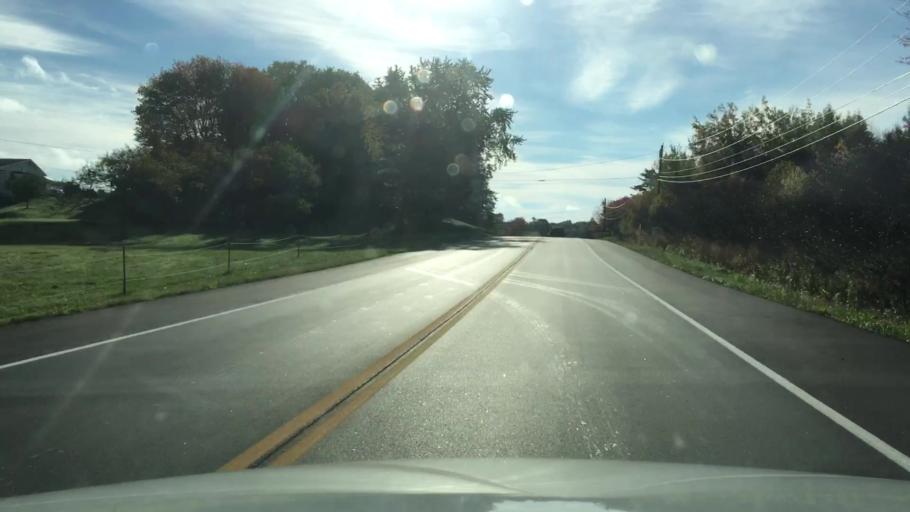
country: US
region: Maine
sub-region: Knox County
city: Warren
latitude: 44.0991
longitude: -69.2467
